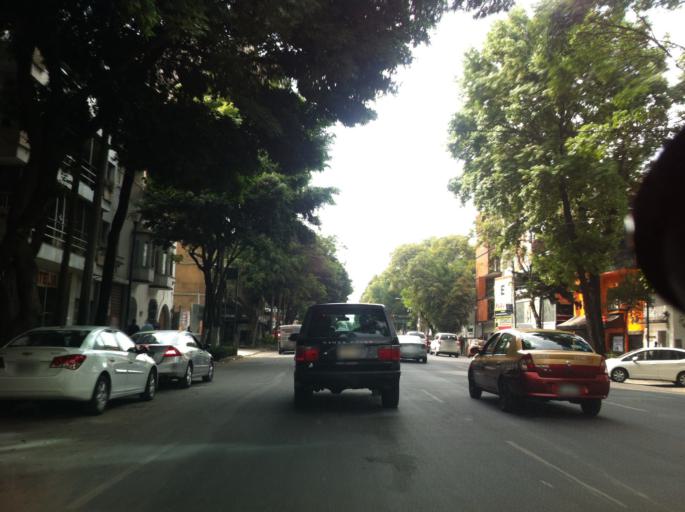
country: MX
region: Mexico City
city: Cuauhtemoc
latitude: 19.4289
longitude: -99.1687
